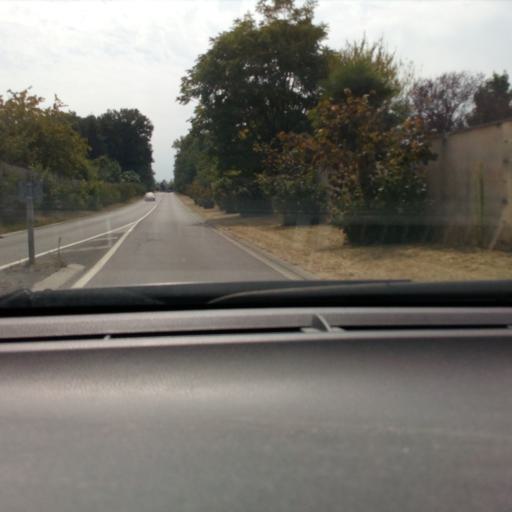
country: FR
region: Poitou-Charentes
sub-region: Departement de la Charente
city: Fleac
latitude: 45.6765
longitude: 0.0991
